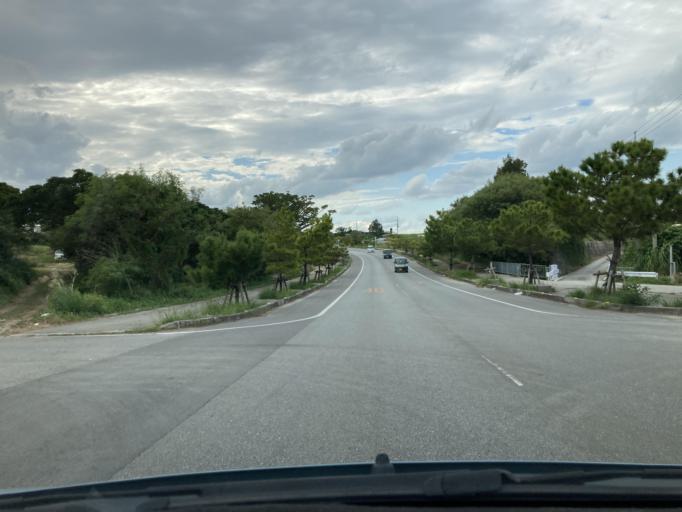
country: JP
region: Okinawa
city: Katsuren-haebaru
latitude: 26.3298
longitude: 127.8897
